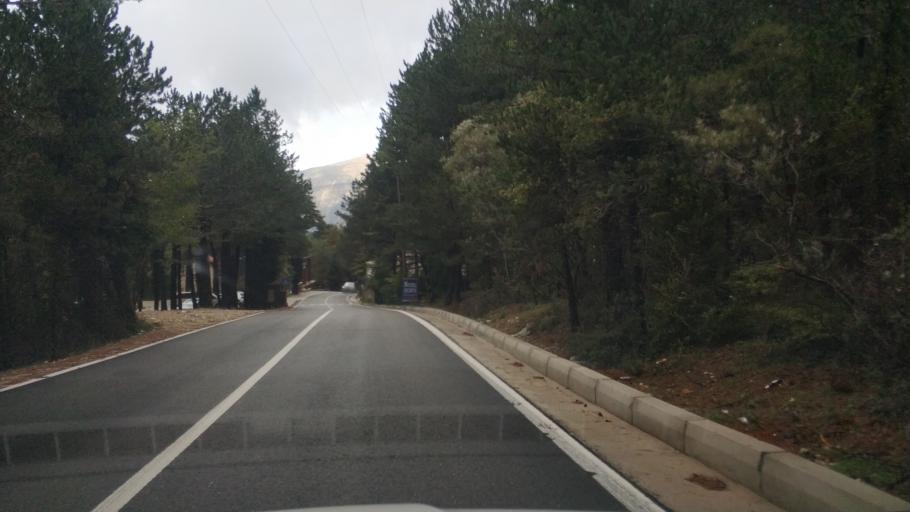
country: AL
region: Vlore
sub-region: Rrethi i Vlores
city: Brataj
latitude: 40.2128
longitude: 19.5792
